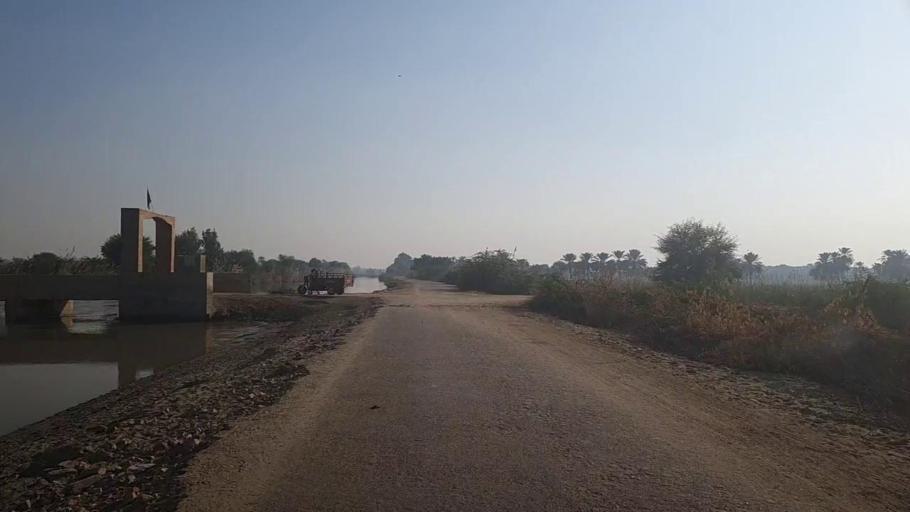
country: PK
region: Sindh
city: Bozdar
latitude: 27.2496
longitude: 68.6775
